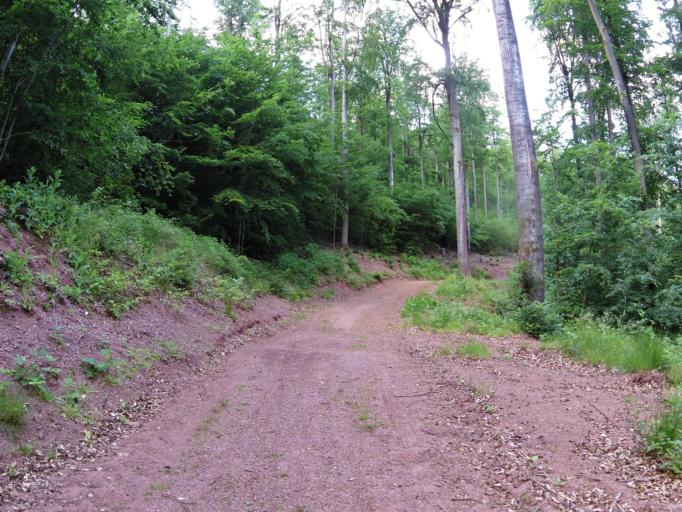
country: DE
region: Thuringia
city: Wolfsburg-Unkeroda
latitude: 50.9246
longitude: 10.3050
